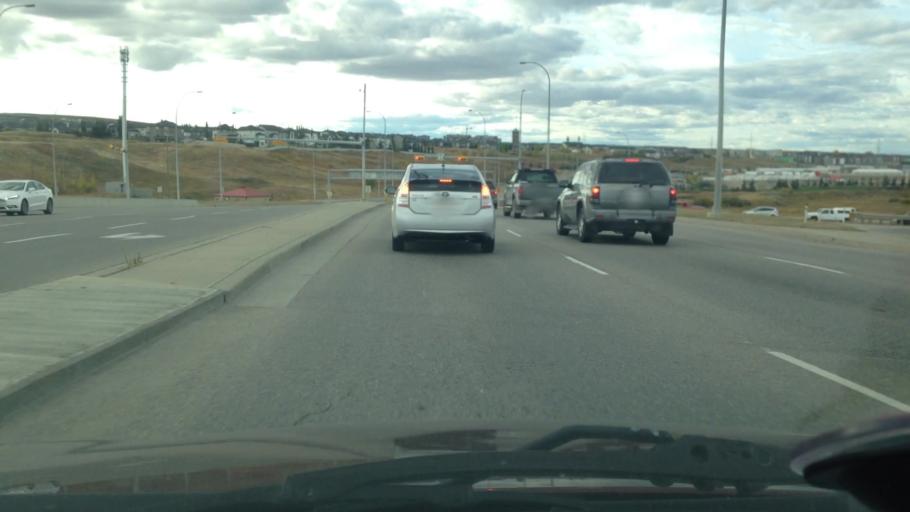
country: CA
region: Alberta
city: Calgary
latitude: 51.1571
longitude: -114.1168
